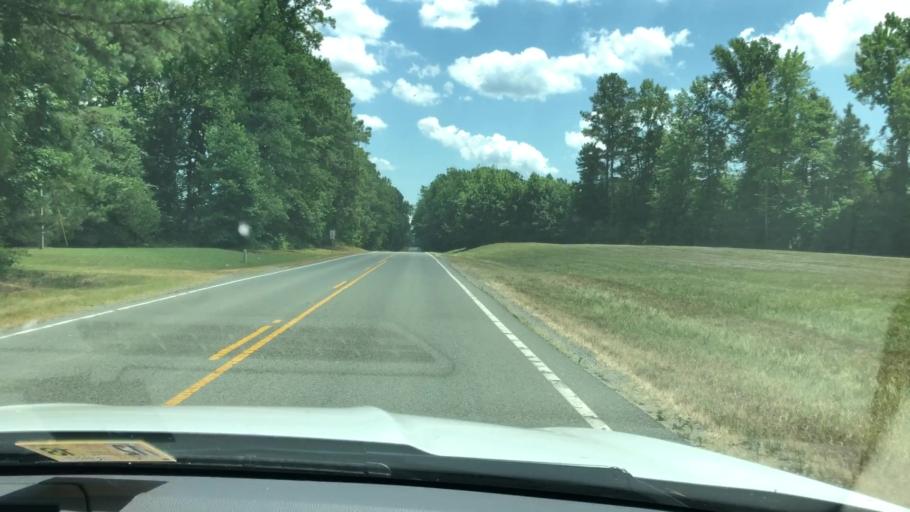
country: US
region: Virginia
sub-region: Lancaster County
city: Lancaster
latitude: 37.8099
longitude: -76.5420
